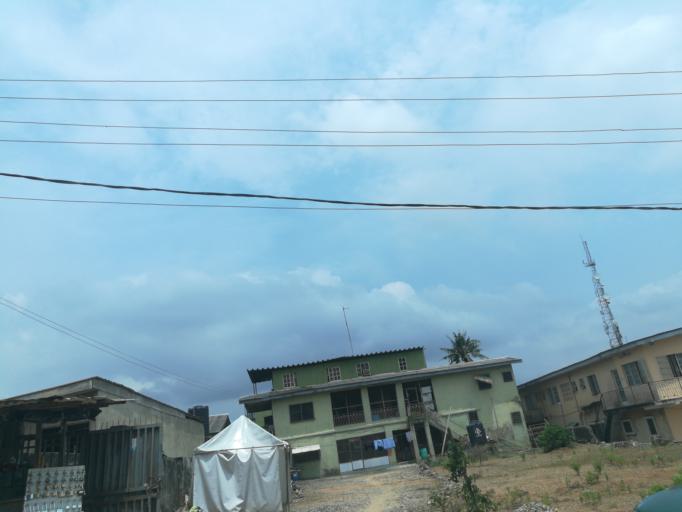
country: NG
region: Lagos
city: Ojota
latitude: 6.5918
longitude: 3.3625
